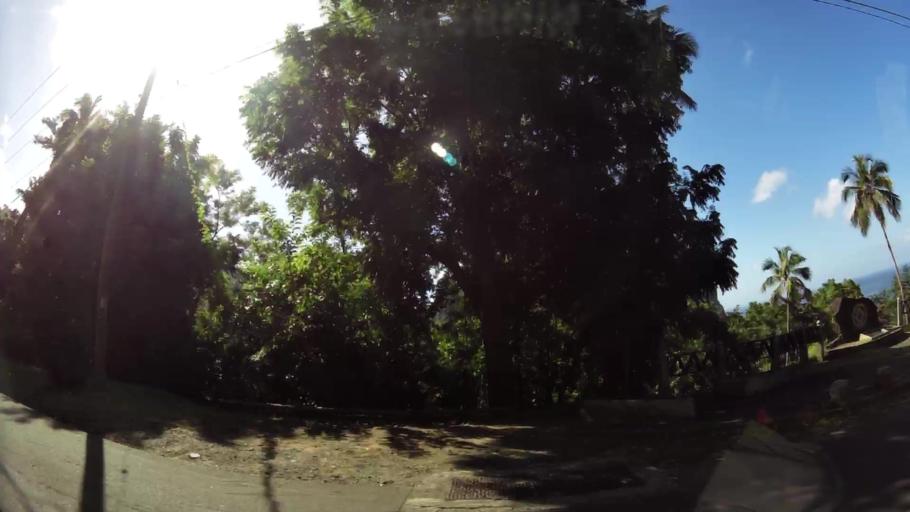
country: LC
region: Soufriere
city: Soufriere
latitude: 13.8458
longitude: -61.0599
